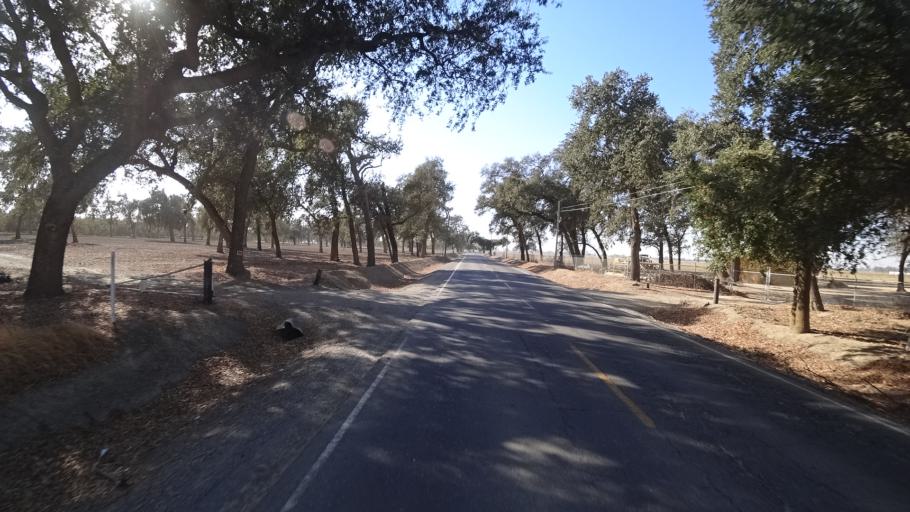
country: US
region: California
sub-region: Yolo County
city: Woodland
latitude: 38.7351
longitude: -121.7606
